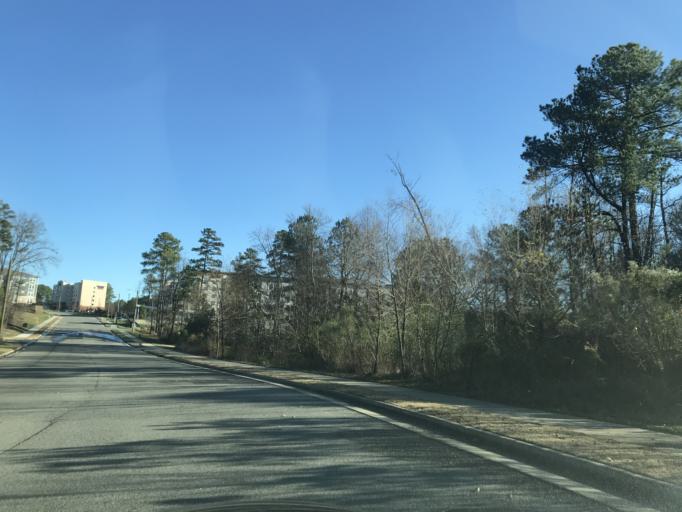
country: US
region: North Carolina
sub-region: Wake County
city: Morrisville
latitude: 35.8968
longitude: -78.8091
